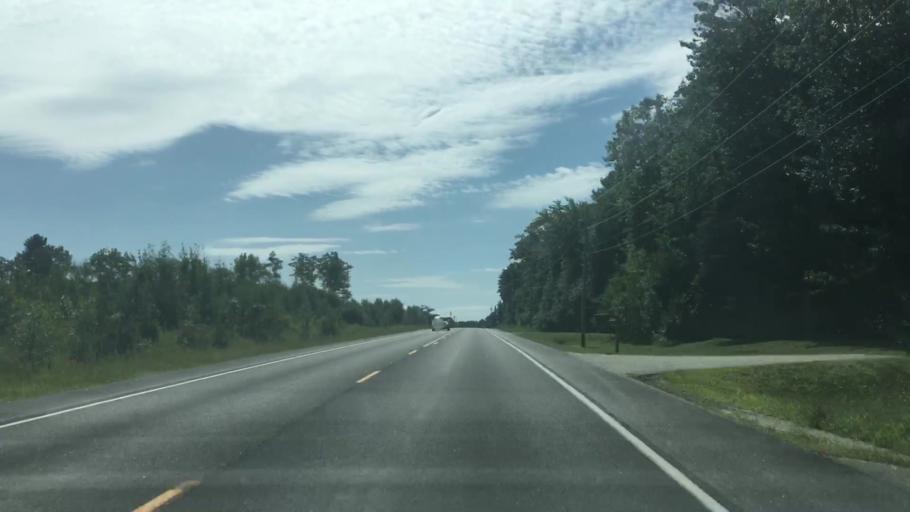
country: US
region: Maine
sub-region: Androscoggin County
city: Lisbon
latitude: 44.0654
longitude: -70.0842
